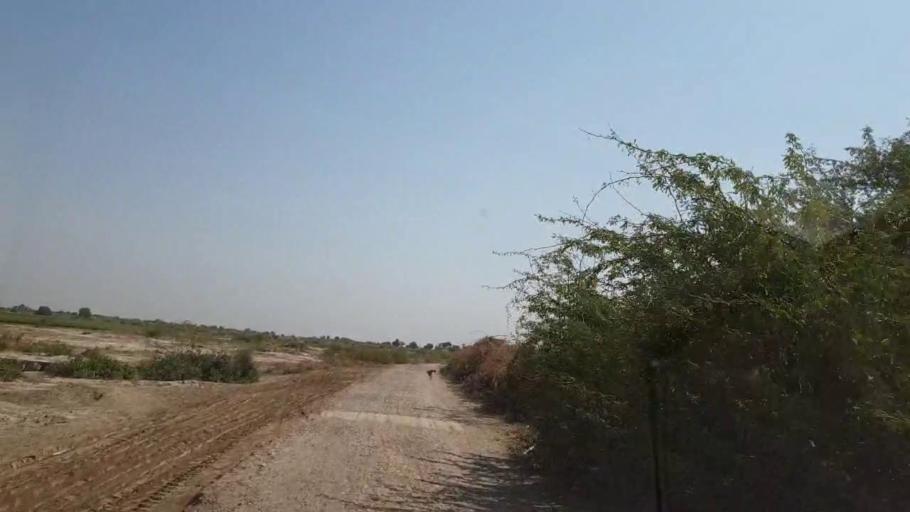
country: PK
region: Sindh
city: Kunri
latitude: 25.0902
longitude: 69.5307
